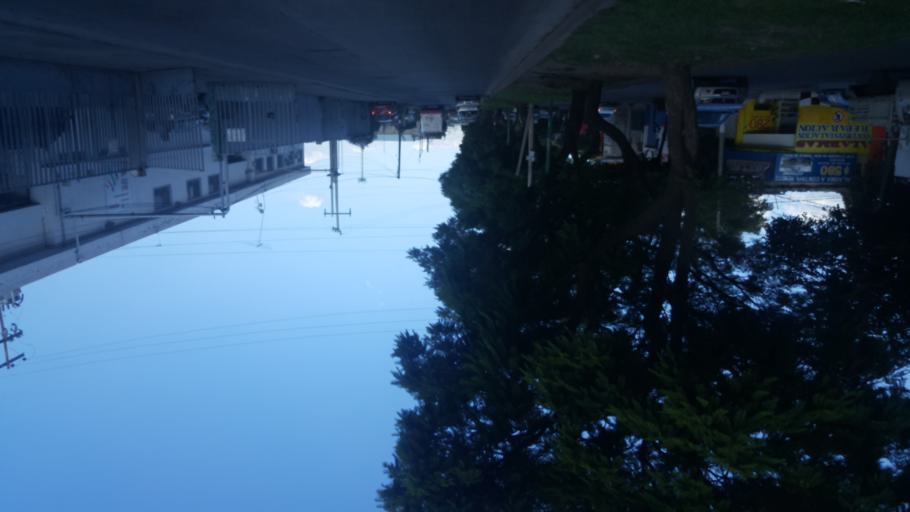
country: MX
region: Guanajuato
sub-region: Leon
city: San Jose de Duran (Los Troncoso)
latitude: 21.0921
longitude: -101.6825
